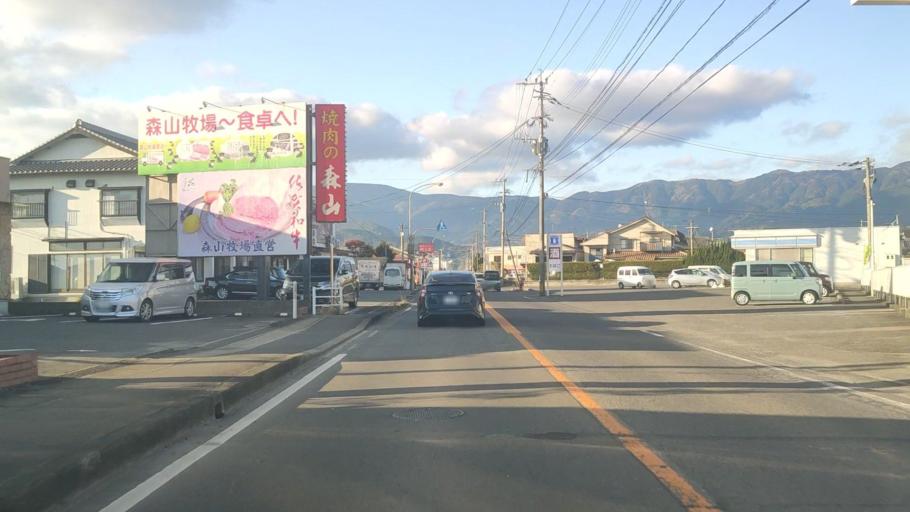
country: JP
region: Saga Prefecture
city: Saga-shi
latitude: 33.2809
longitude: 130.2122
